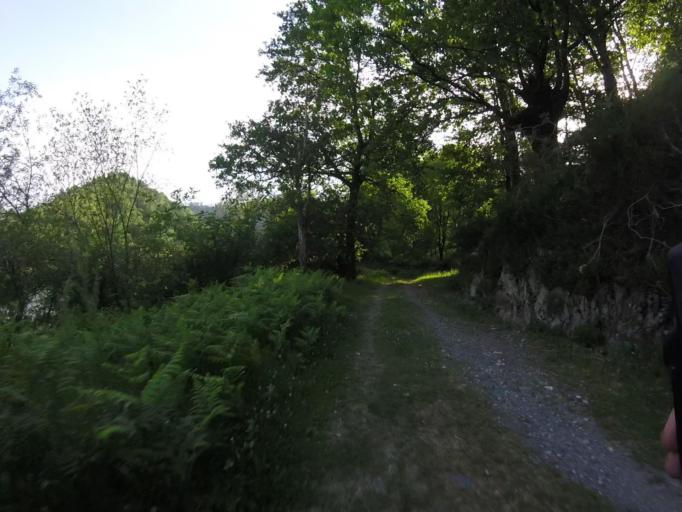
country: ES
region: Navarre
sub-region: Provincia de Navarra
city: Arano
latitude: 43.2308
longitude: -1.8690
